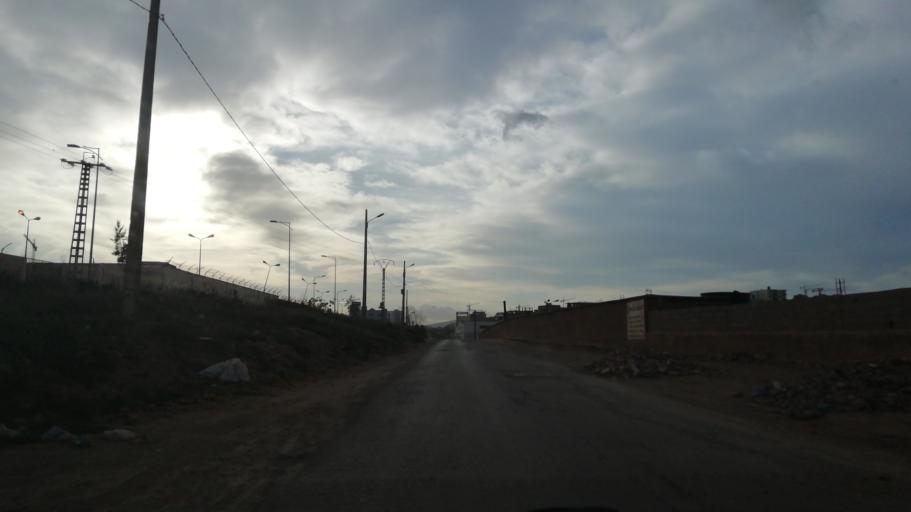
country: DZ
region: Oran
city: Bir el Djir
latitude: 35.7172
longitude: -0.5624
